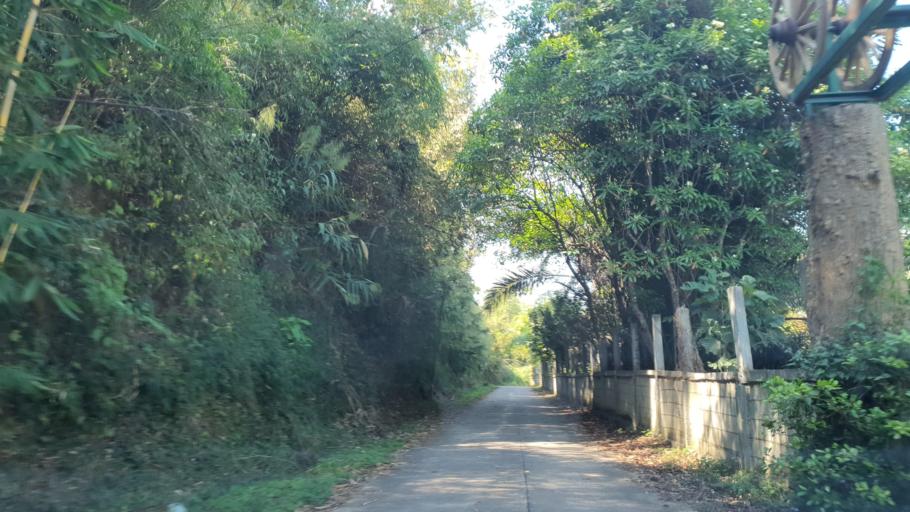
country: TH
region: Lampang
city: Wang Nuea
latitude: 19.1861
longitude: 99.4982
